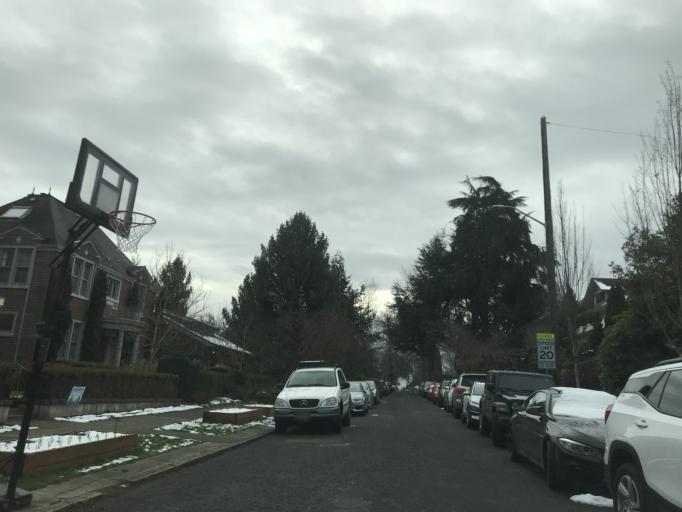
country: US
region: Washington
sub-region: King County
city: Seattle
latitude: 47.6278
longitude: -122.3036
